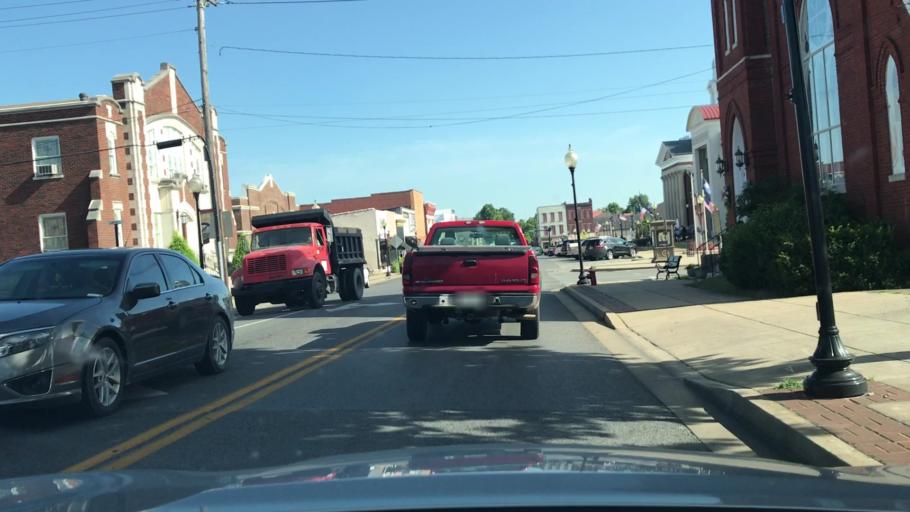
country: US
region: Kentucky
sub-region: Muhlenberg County
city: Greenville
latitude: 37.1992
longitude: -87.1782
